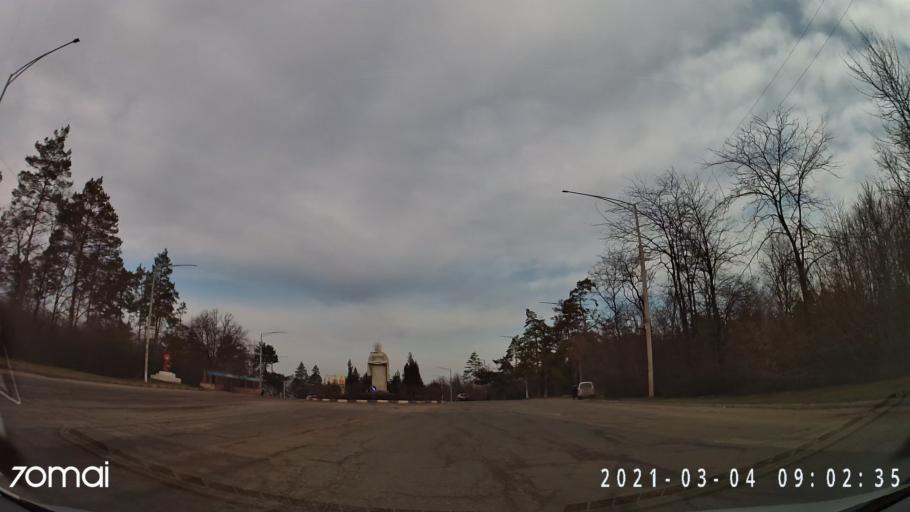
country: MD
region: Balti
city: Balti
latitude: 47.7442
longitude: 27.9534
